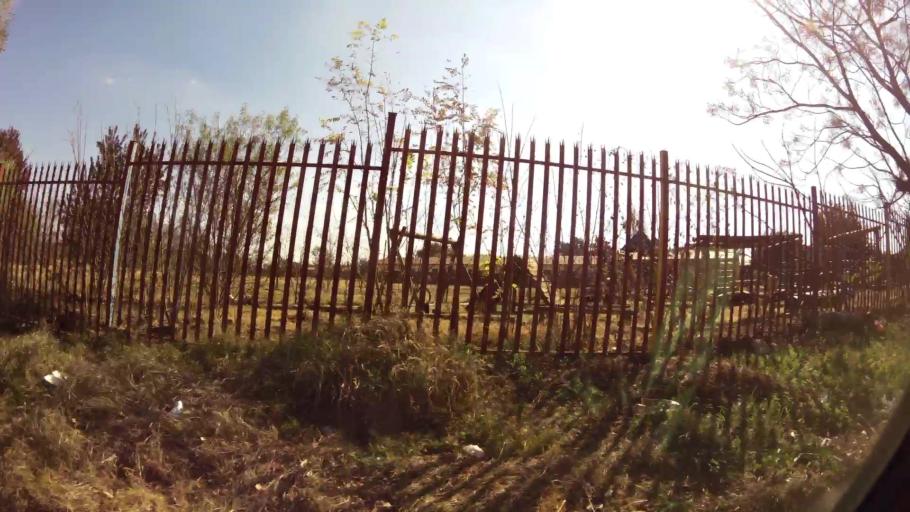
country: ZA
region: Gauteng
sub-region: City of Johannesburg Metropolitan Municipality
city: Soweto
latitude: -26.2380
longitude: 27.8819
